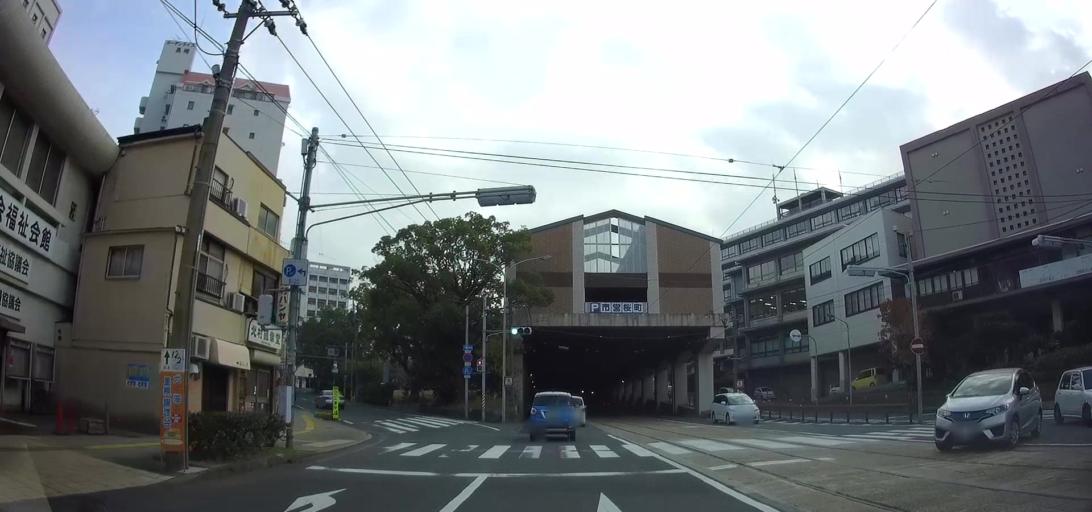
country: JP
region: Nagasaki
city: Nagasaki-shi
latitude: 32.7508
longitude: 129.8766
